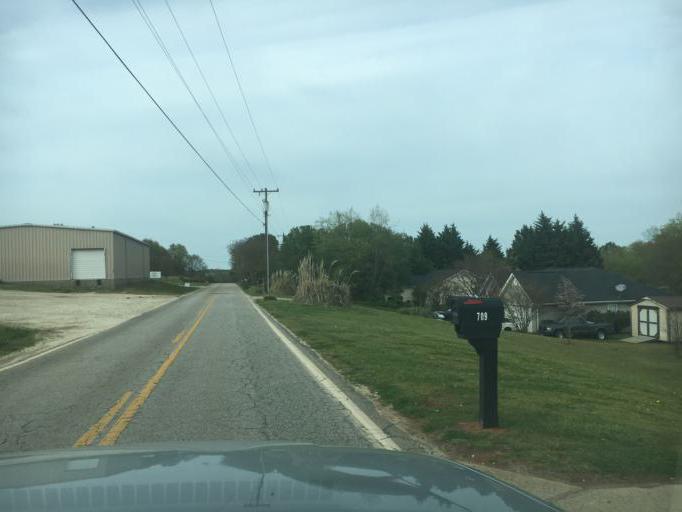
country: US
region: South Carolina
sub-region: Spartanburg County
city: Duncan
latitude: 34.9219
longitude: -82.1654
